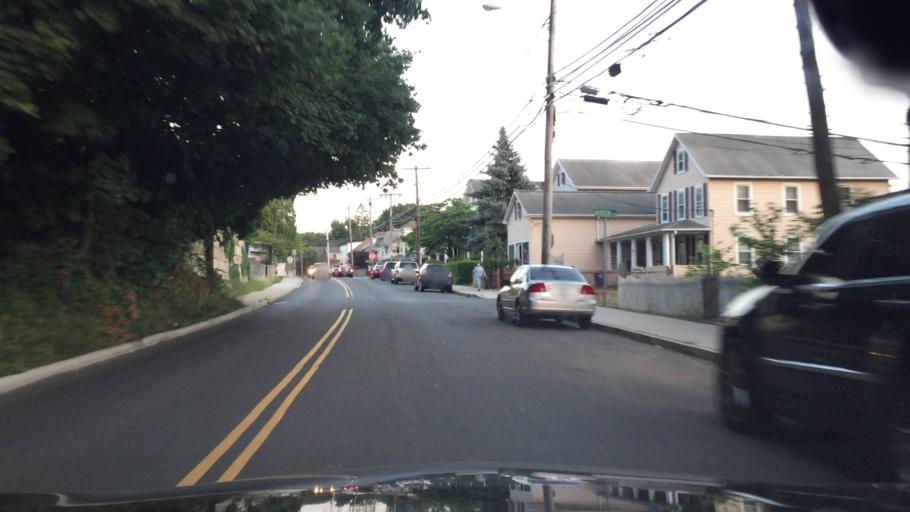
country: US
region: Connecticut
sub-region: Fairfield County
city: Norwalk
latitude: 41.1010
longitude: -73.4291
